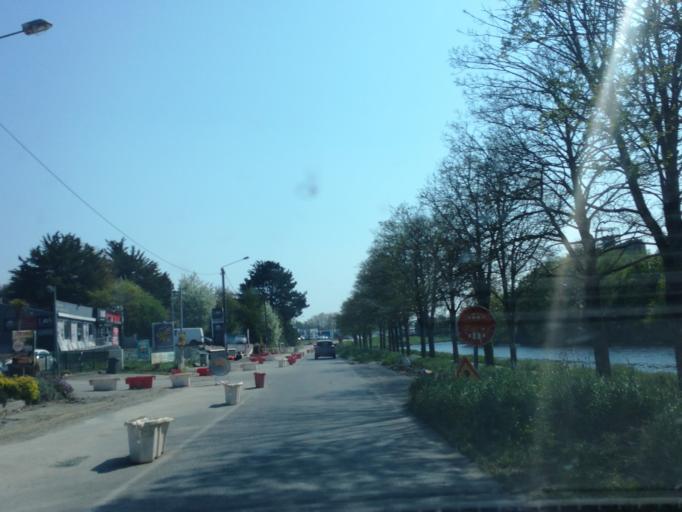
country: FR
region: Brittany
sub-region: Departement du Morbihan
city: Le Sourn
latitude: 48.0489
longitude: -2.9586
